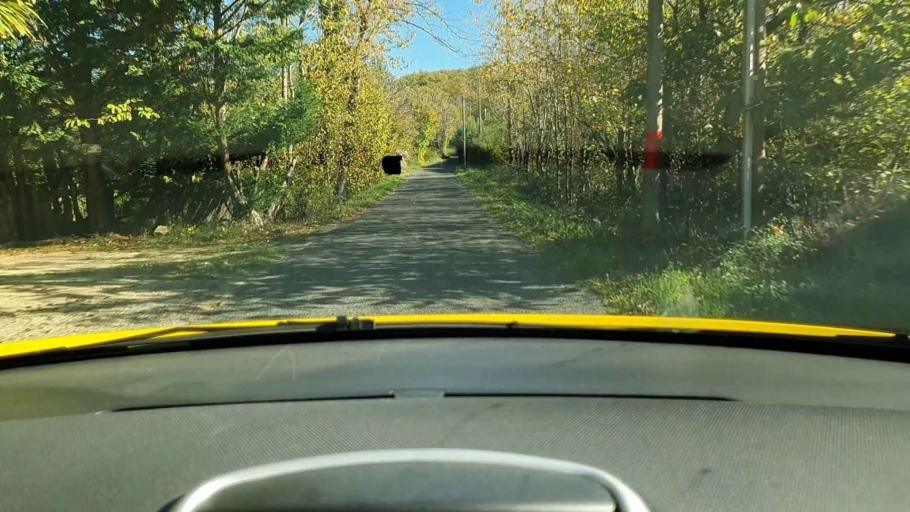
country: FR
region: Languedoc-Roussillon
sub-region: Departement du Gard
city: Sumene
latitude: 44.0363
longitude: 3.7127
